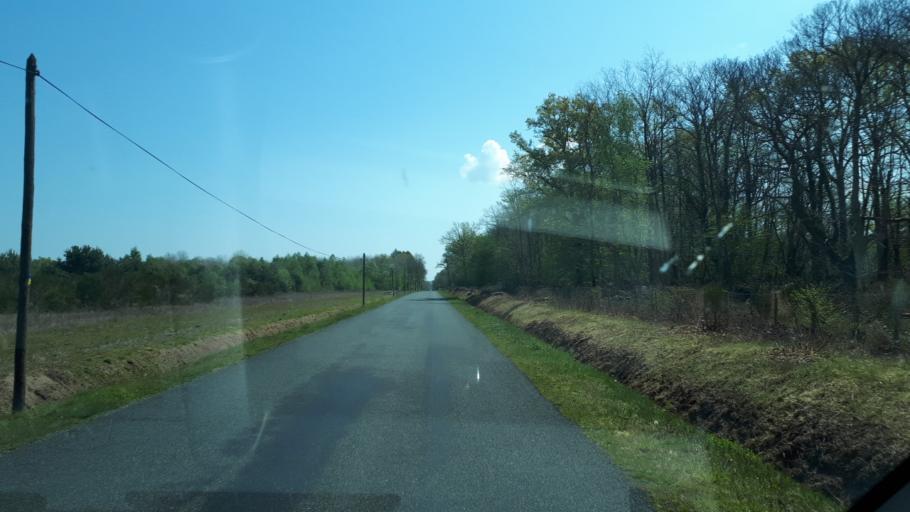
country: FR
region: Centre
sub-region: Departement du Cher
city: Neuvy-sur-Barangeon
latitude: 47.3188
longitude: 2.2124
